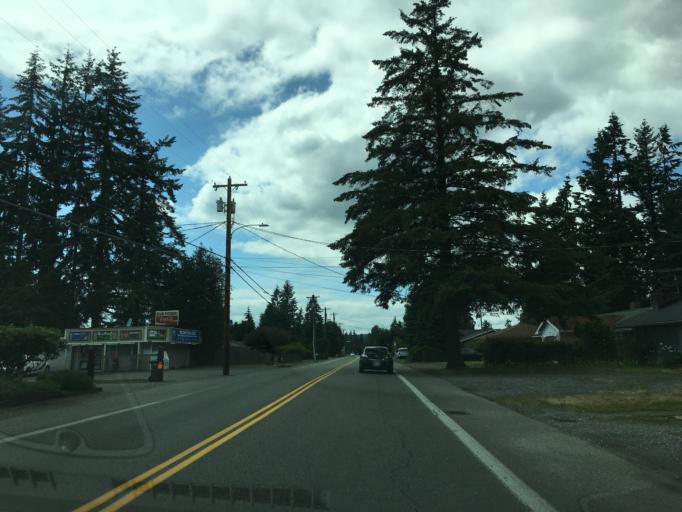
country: US
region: Washington
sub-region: Snohomish County
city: Marysville
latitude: 48.0752
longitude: -122.1581
